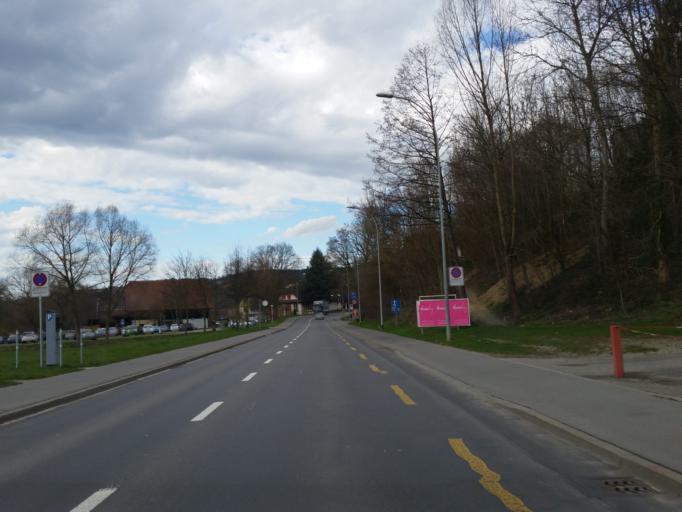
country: CH
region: Lucerne
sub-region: Sursee District
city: Sempach
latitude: 47.1323
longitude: 8.1917
